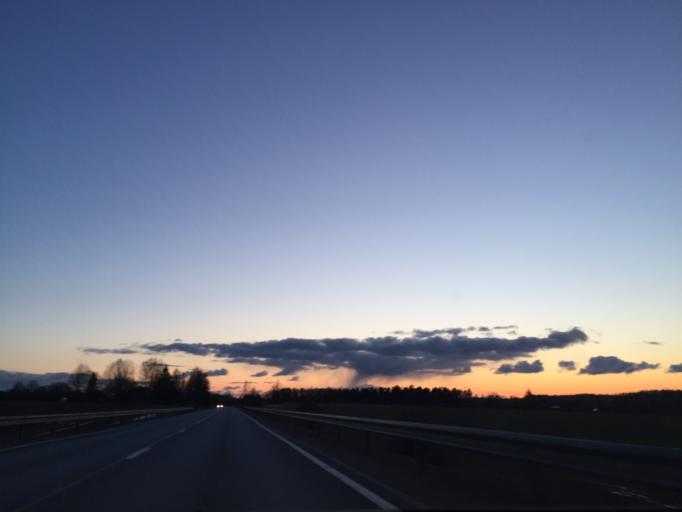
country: LV
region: Krimulda
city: Ragana
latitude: 57.2005
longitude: 24.7566
